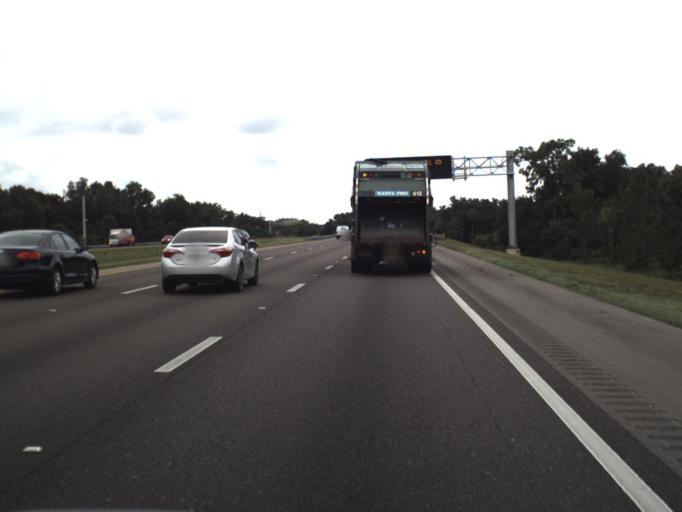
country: US
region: Florida
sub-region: Sarasota County
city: Desoto Lakes
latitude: 27.4158
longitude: -82.4566
